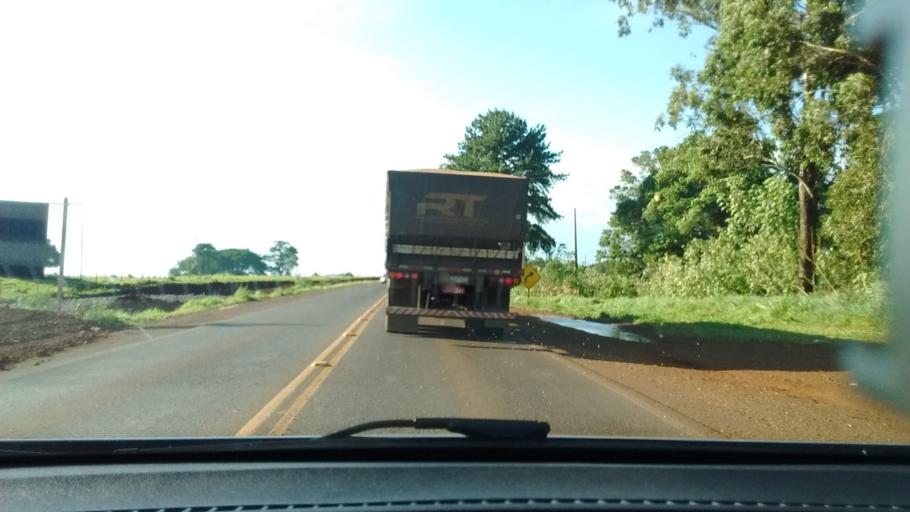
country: BR
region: Parana
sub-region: Cascavel
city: Cascavel
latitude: -25.1863
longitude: -53.6011
